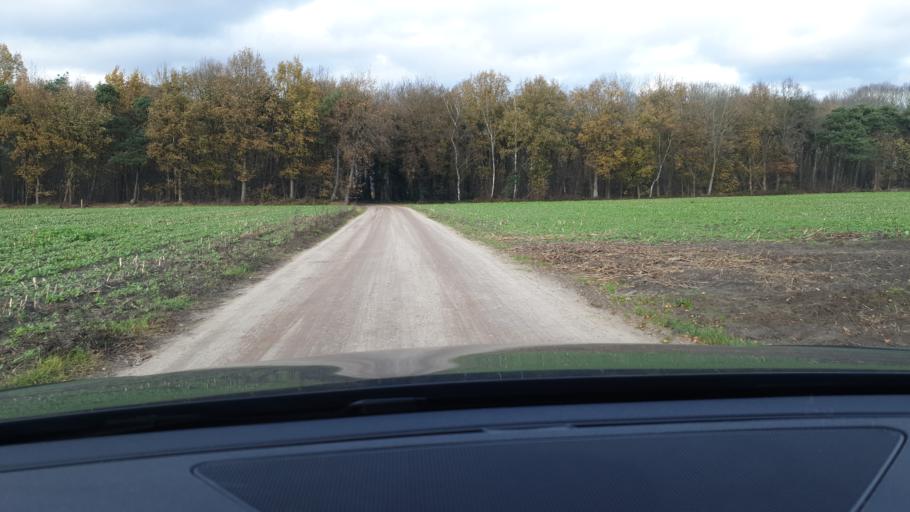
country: NL
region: North Brabant
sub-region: Gemeente Waalre
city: Waalre
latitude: 51.3732
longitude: 5.4382
